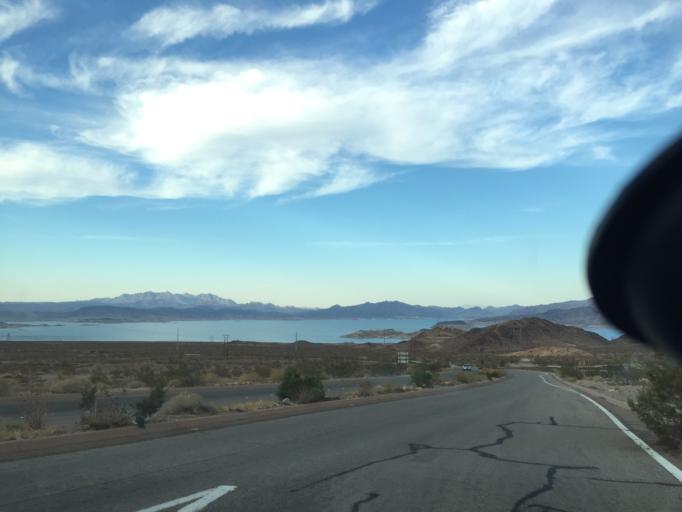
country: US
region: Nevada
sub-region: Clark County
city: Boulder City
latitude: 36.0109
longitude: -114.7960
